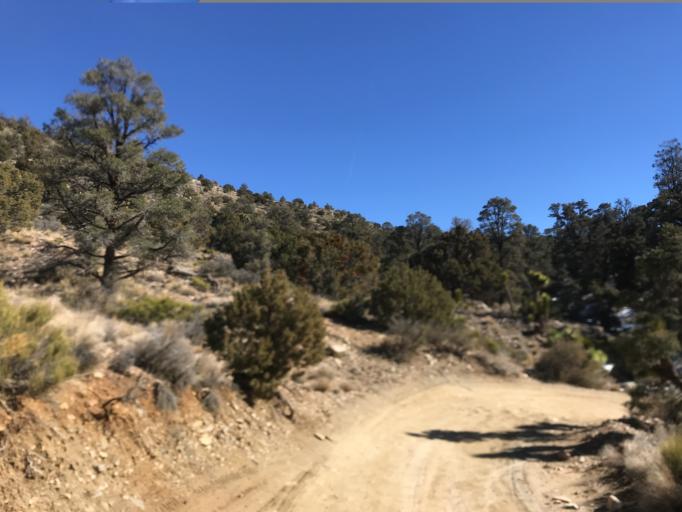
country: US
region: California
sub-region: San Bernardino County
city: Big Bear City
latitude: 34.2367
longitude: -116.6880
